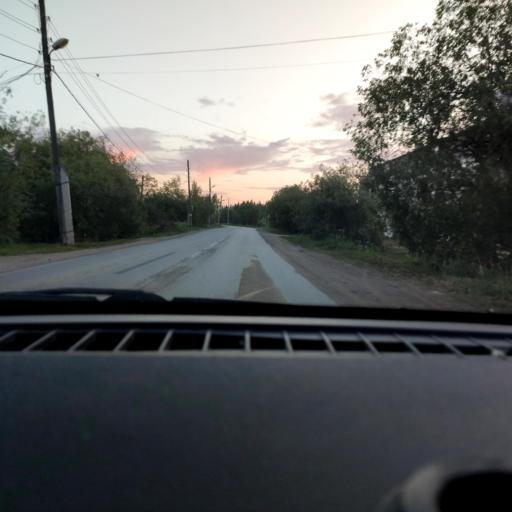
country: RU
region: Perm
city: Kukushtan
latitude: 57.6335
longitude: 56.5245
